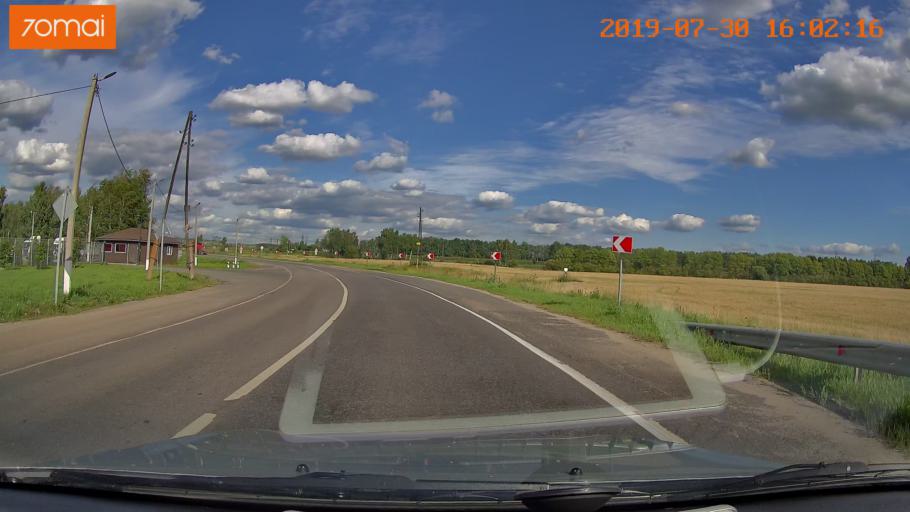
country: RU
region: Moskovskaya
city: Voskresensk
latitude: 55.2876
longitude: 38.6862
